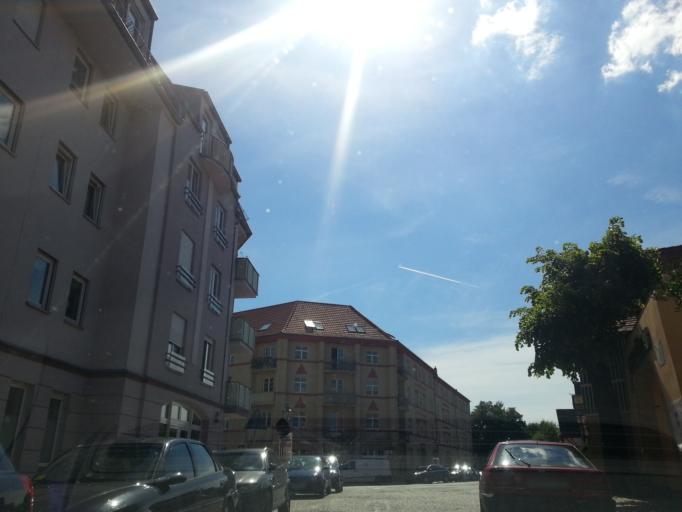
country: DE
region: Saxony
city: Dresden
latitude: 51.0863
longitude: 13.7138
